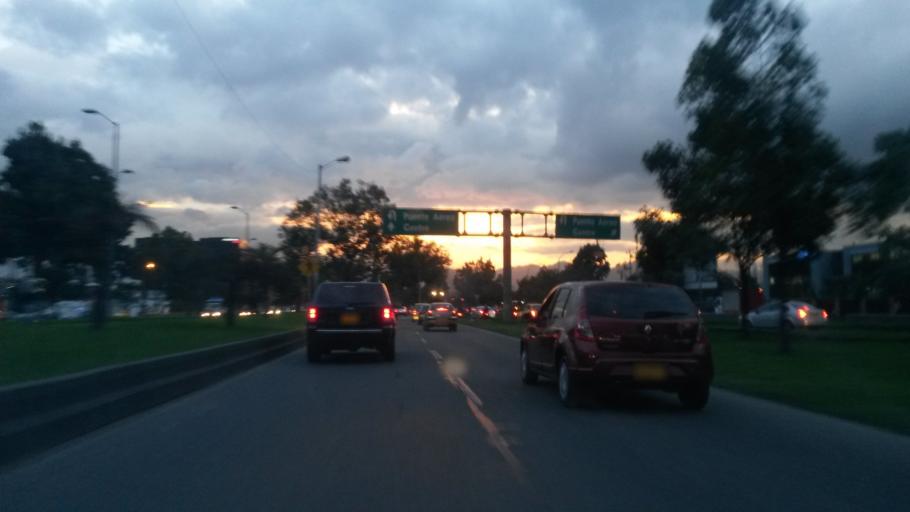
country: CO
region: Cundinamarca
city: Funza
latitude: 4.6889
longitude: -74.1304
